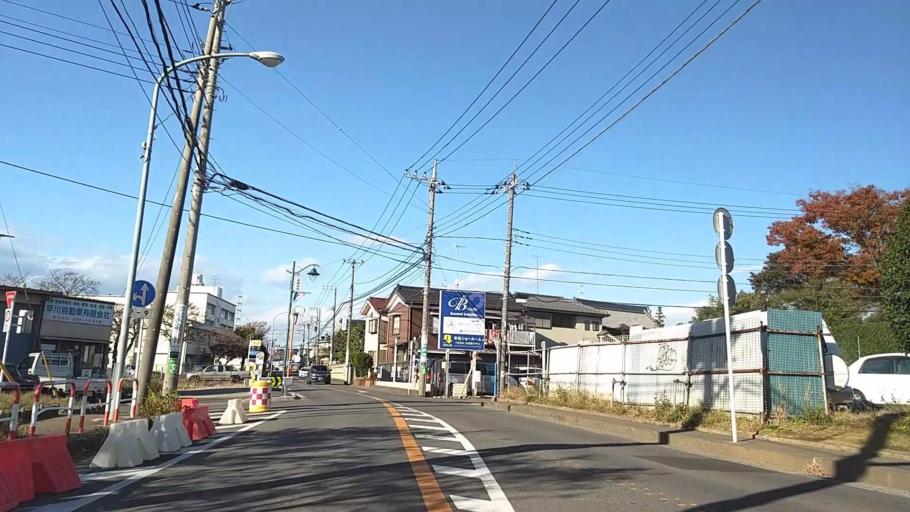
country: JP
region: Tokyo
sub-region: Machida-shi
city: Machida
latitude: 35.5286
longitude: 139.5485
